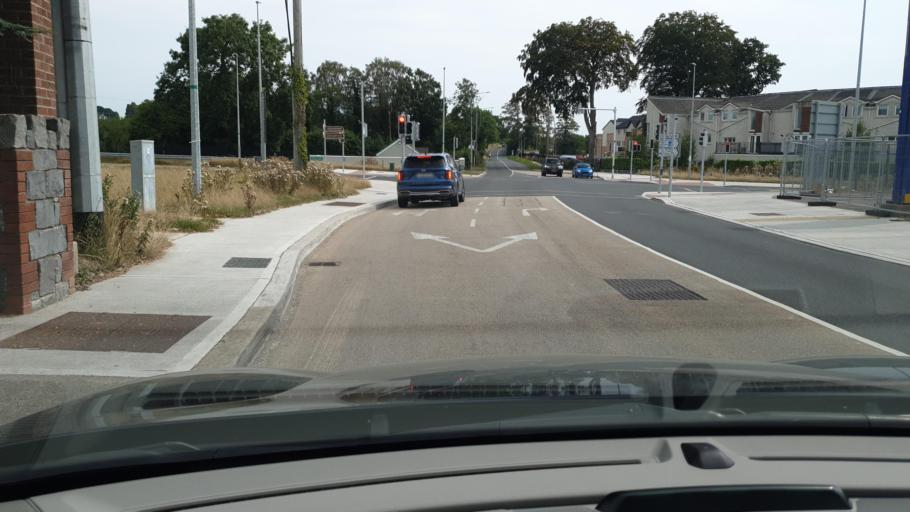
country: IE
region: Leinster
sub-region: An Mhi
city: Navan
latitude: 53.6487
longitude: -6.6546
